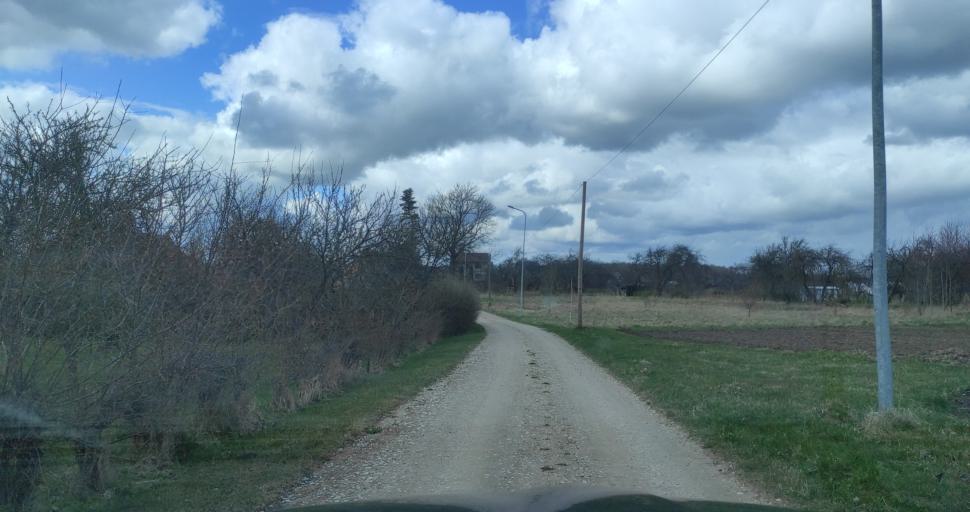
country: LV
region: Aizpute
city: Aizpute
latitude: 56.7191
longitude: 21.5863
